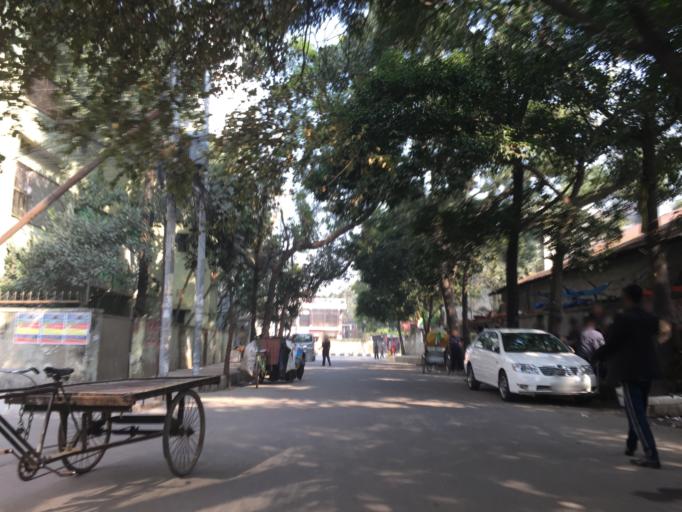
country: BD
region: Dhaka
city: Paltan
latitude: 23.7895
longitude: 90.4093
